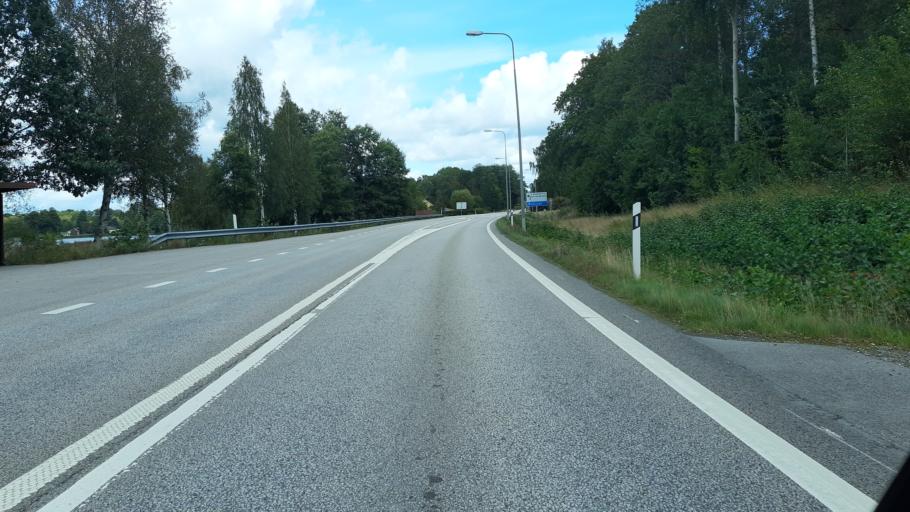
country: SE
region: Kronoberg
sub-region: Tingsryds Kommun
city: Tingsryd
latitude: 56.5101
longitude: 15.1502
